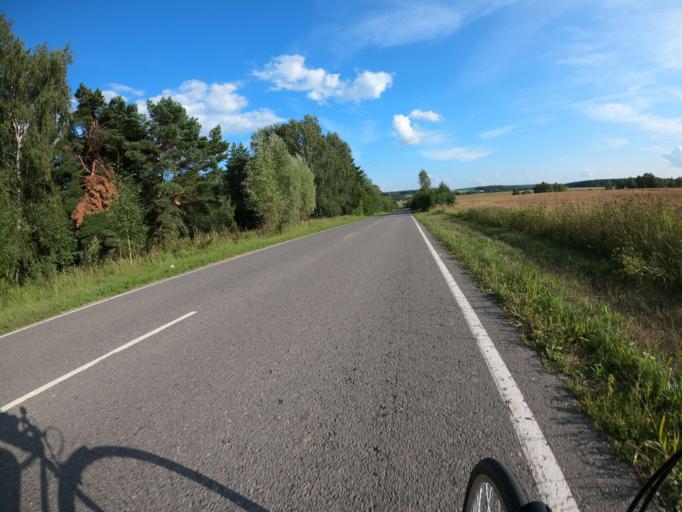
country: RU
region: Moskovskaya
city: Meshcherino
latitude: 55.1500
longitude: 38.4339
